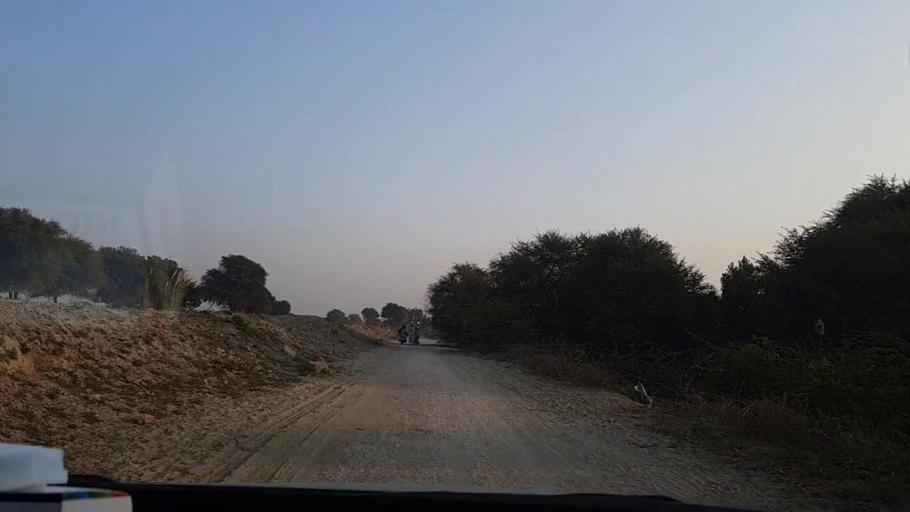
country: PK
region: Sindh
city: Tando Ghulam Ali
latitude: 25.1807
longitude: 68.9242
